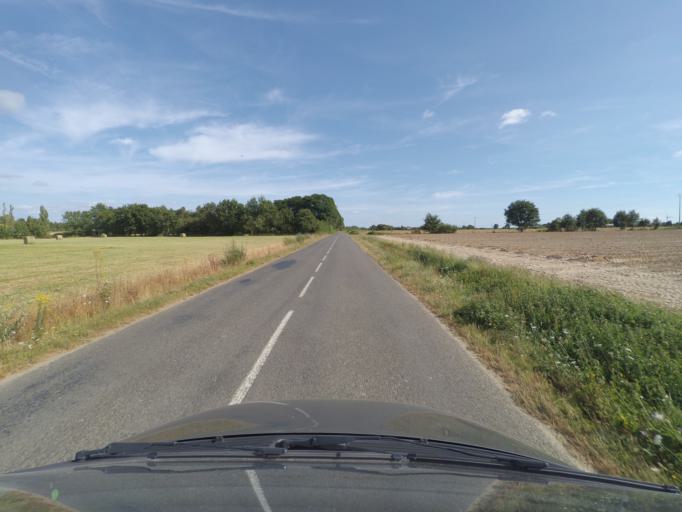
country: FR
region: Pays de la Loire
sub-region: Departement de la Loire-Atlantique
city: La Planche
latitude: 47.0214
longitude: -1.4601
